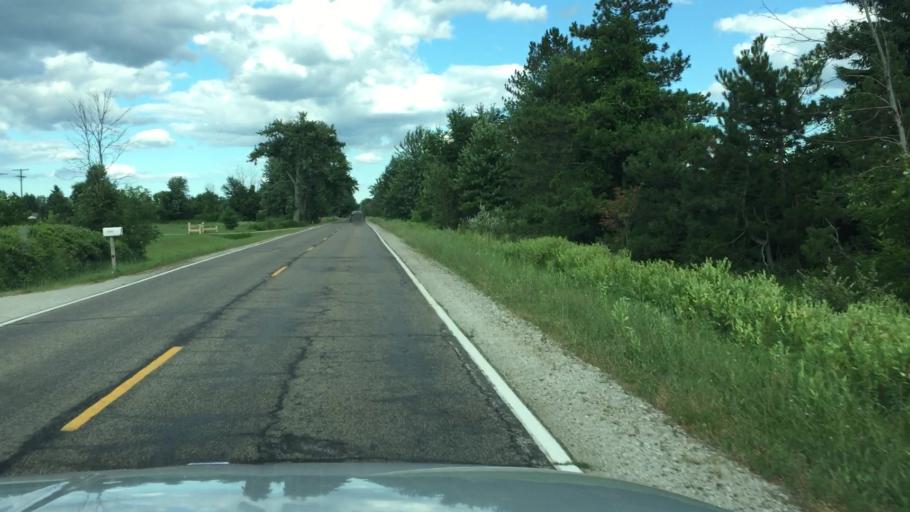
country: US
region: Michigan
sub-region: Saint Clair County
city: Yale
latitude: 43.1280
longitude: -82.8899
